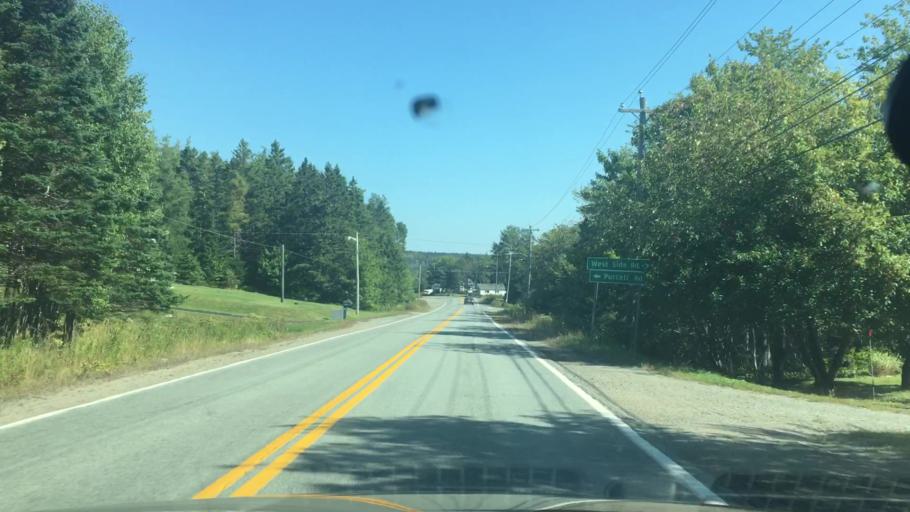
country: CA
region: Nova Scotia
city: New Glasgow
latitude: 44.9122
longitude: -62.5411
